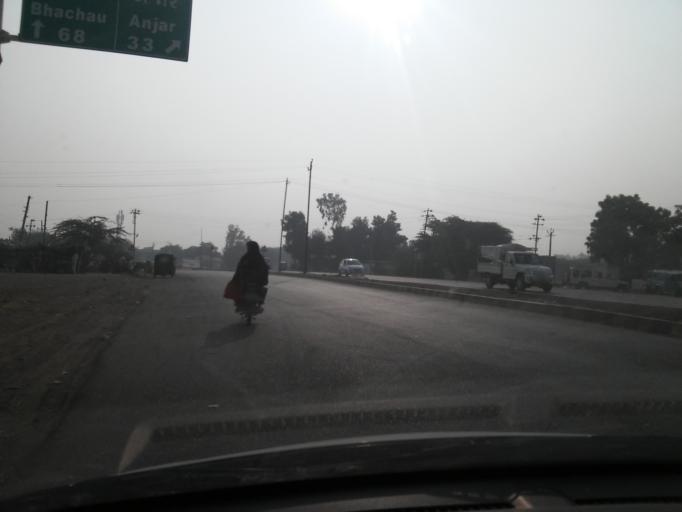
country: IN
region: Gujarat
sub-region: Kachchh
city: Bhuj
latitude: 23.2298
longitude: 69.7586
